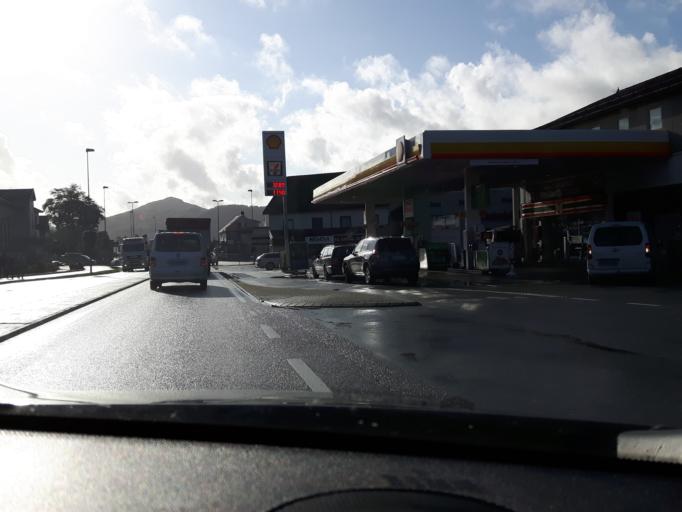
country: NO
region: Rogaland
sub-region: Gjesdal
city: Algard
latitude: 58.7675
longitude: 5.8608
